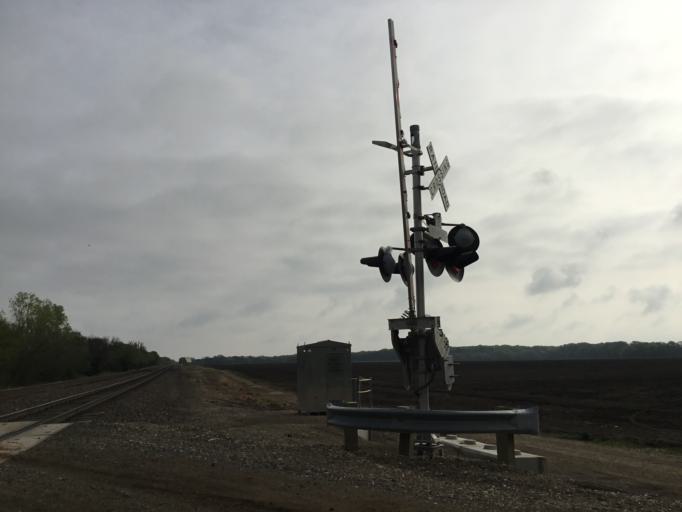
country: US
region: Kansas
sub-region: Butler County
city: Augusta
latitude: 37.7269
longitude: -96.9170
